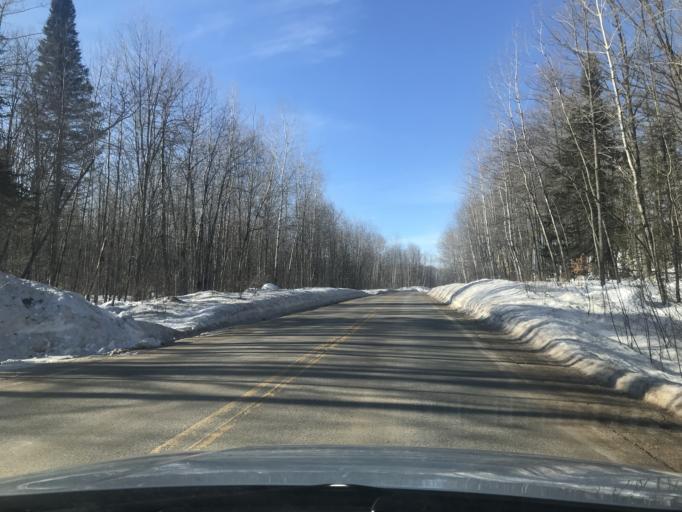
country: US
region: Wisconsin
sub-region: Forest County
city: Crandon
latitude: 45.4188
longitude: -88.4173
